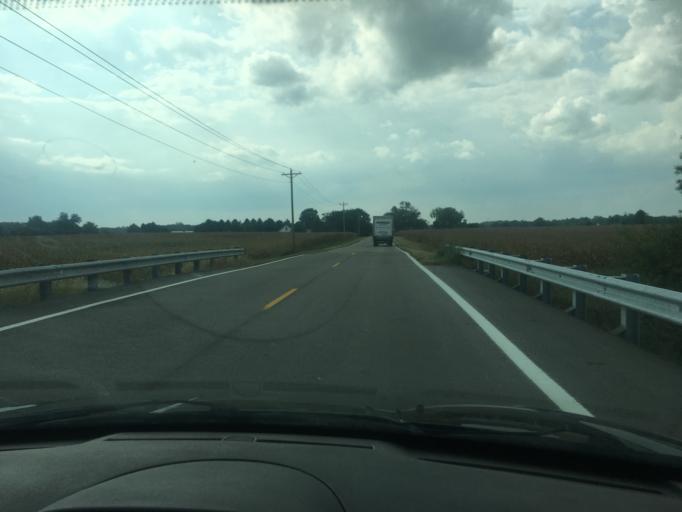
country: US
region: Ohio
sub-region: Champaign County
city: Urbana
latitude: 40.1589
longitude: -83.8082
